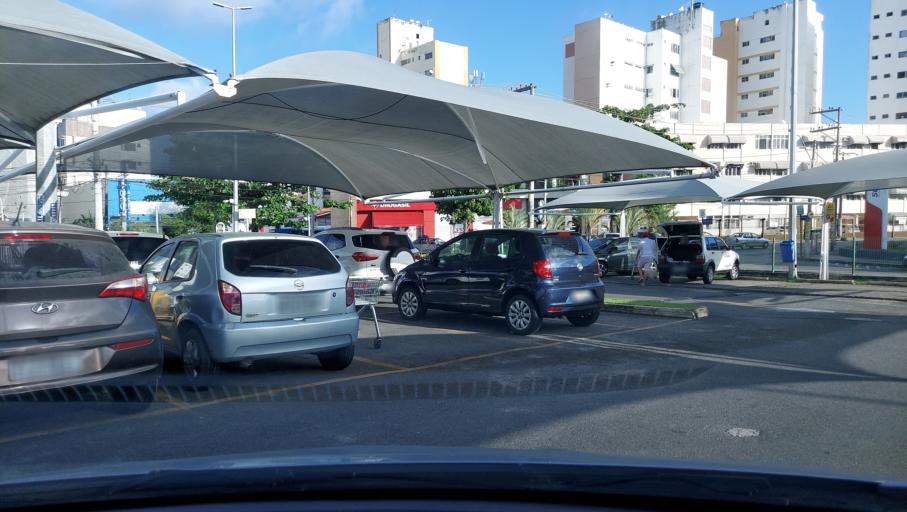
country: BR
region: Bahia
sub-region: Salvador
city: Salvador
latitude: -12.9923
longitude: -38.4486
